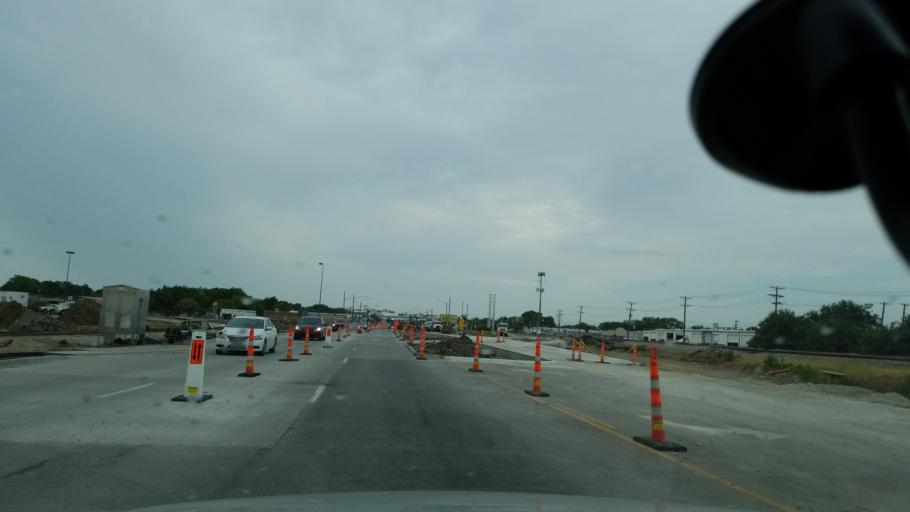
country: US
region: Texas
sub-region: Dallas County
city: Grand Prairie
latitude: 32.7452
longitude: -96.9849
